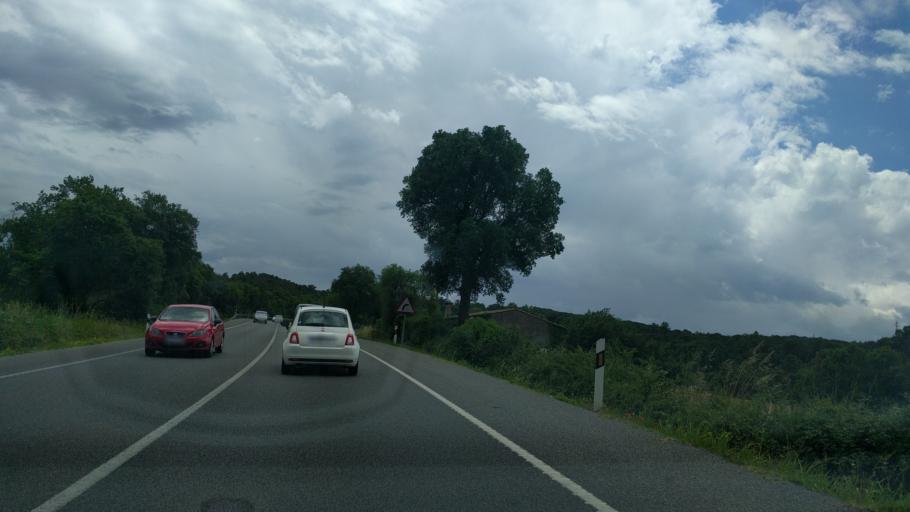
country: ES
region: Catalonia
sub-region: Provincia de Girona
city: Macanet de la Selva
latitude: 41.7528
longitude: 2.7560
